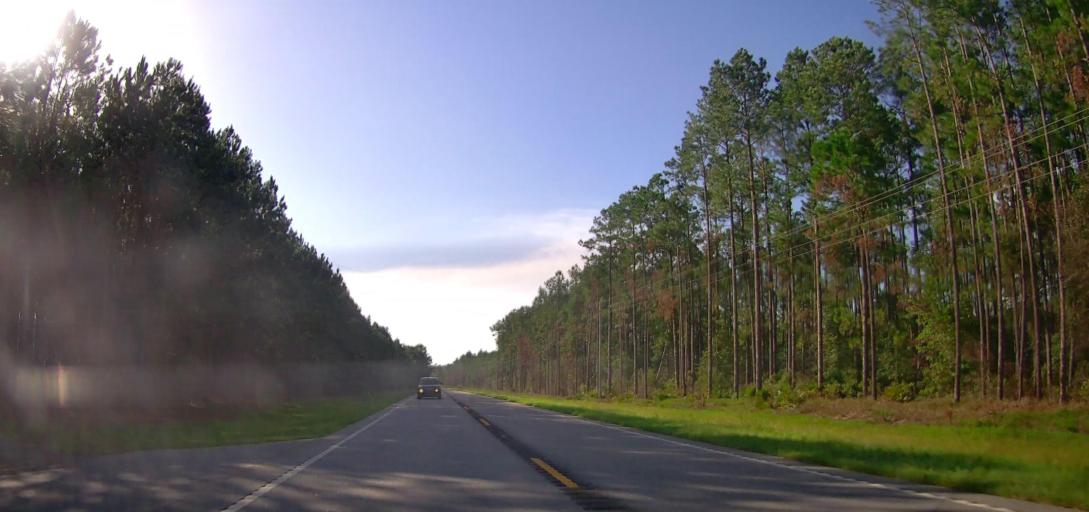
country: US
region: Georgia
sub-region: Coffee County
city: Nicholls
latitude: 31.4470
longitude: -82.7233
